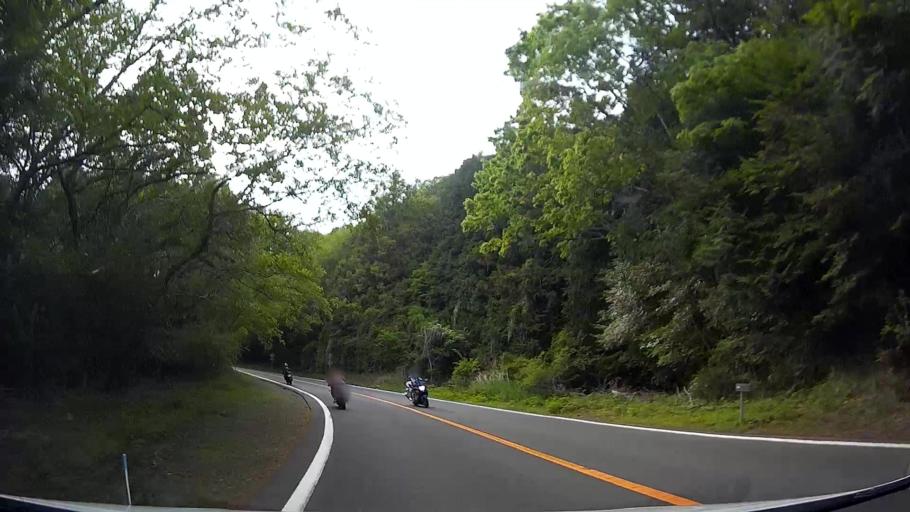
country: JP
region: Shizuoka
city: Ito
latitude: 34.9831
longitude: 139.0558
